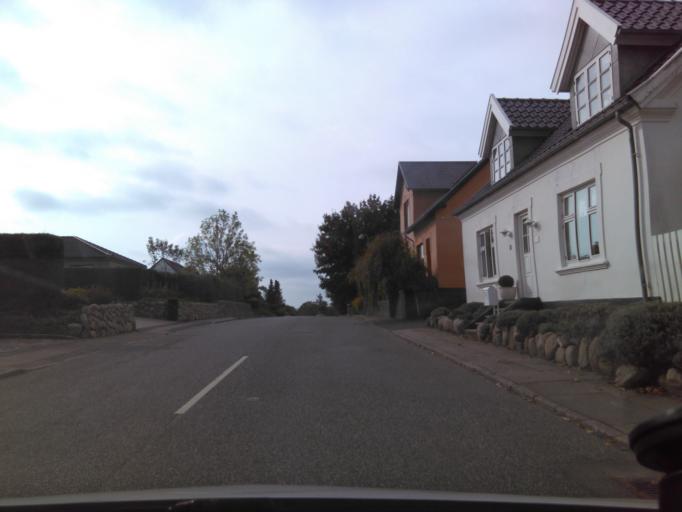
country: DK
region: Capital Region
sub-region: Ballerup Kommune
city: Malov
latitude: 55.7845
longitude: 12.3232
